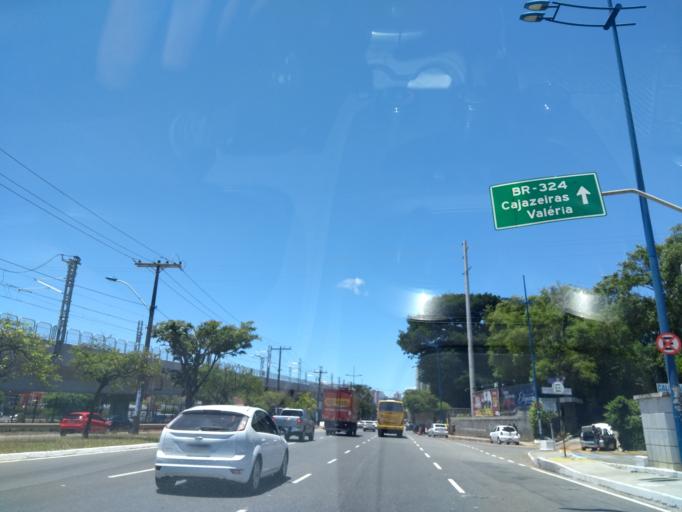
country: BR
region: Bahia
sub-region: Salvador
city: Salvador
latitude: -12.9789
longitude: -38.4677
